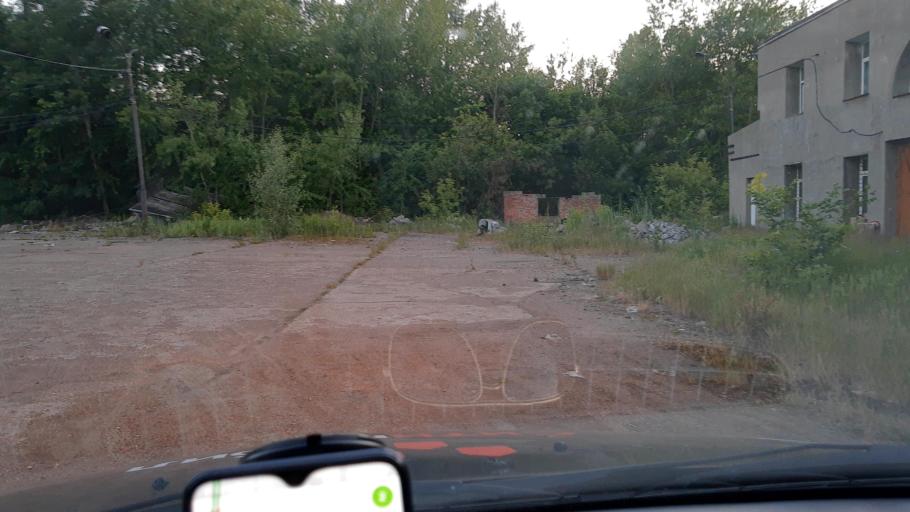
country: RU
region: Bashkortostan
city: Blagoveshchensk
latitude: 54.9081
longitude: 56.0824
